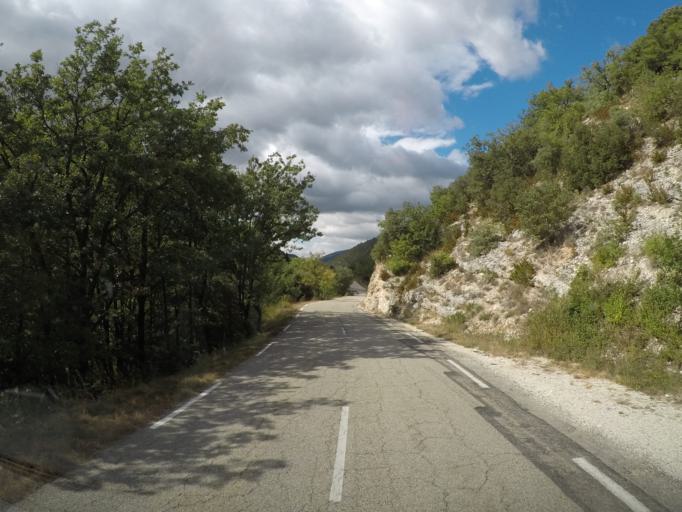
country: FR
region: Rhone-Alpes
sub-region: Departement de la Drome
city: Buis-les-Baronnies
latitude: 44.1901
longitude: 5.3354
